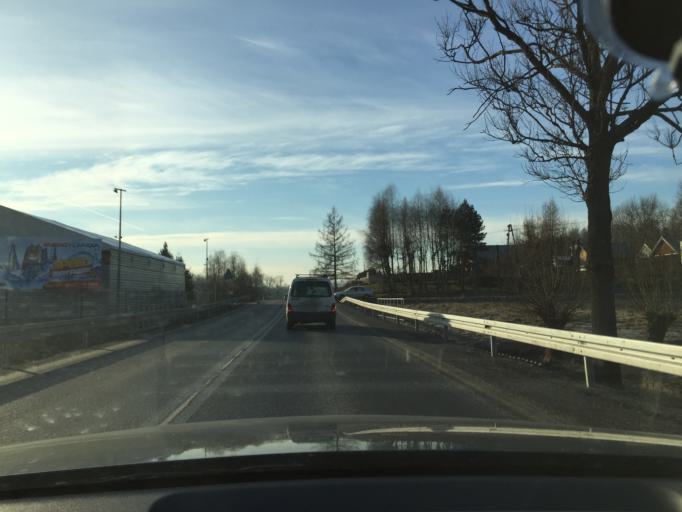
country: PL
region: Lesser Poland Voivodeship
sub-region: Powiat myslenicki
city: Krzywaczka
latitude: 49.9032
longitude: 19.8514
